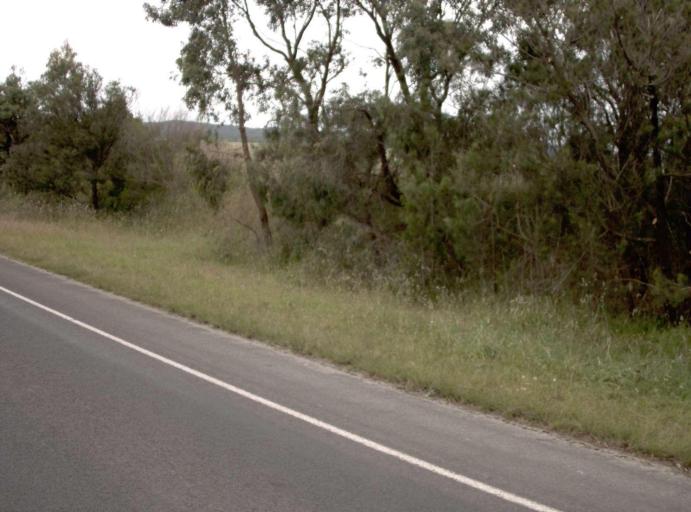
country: AU
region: Victoria
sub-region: Cardinia
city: Koo-Wee-Rup
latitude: -38.3061
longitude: 145.5718
